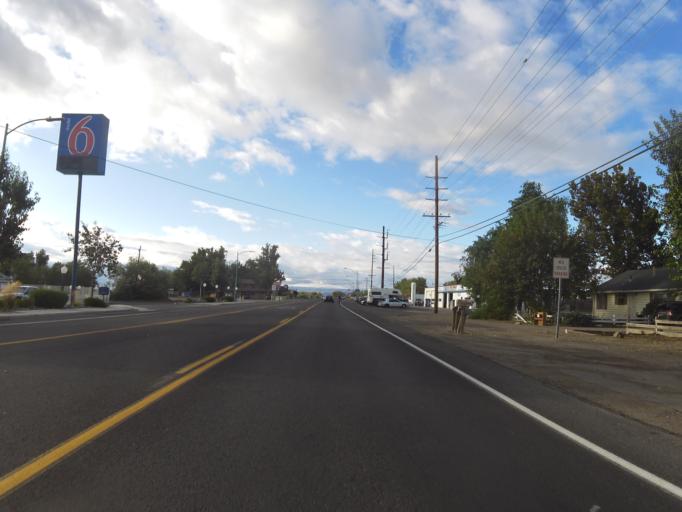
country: US
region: Nevada
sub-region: Churchill County
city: Fallon
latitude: 39.4625
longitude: -118.7816
